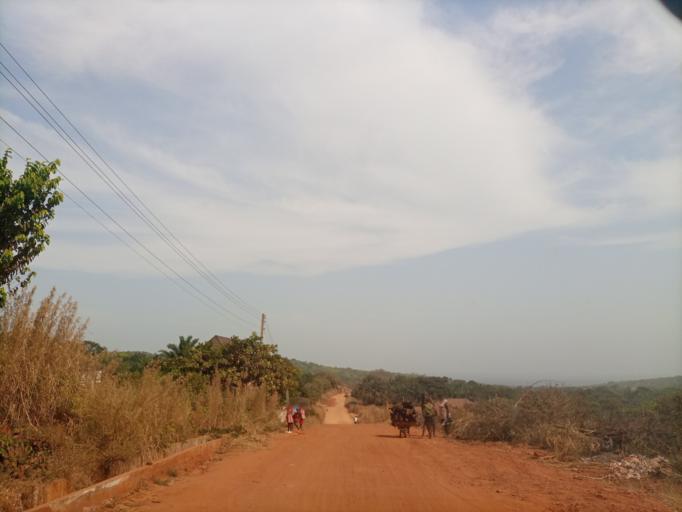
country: NG
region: Enugu
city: Opi
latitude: 6.8219
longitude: 7.4763
